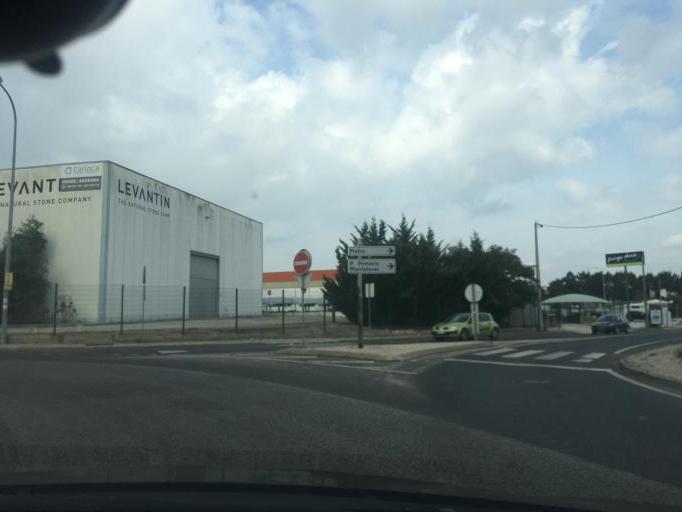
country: PT
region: Lisbon
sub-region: Sintra
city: Pero Pinheiro
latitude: 38.8351
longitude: -9.3559
